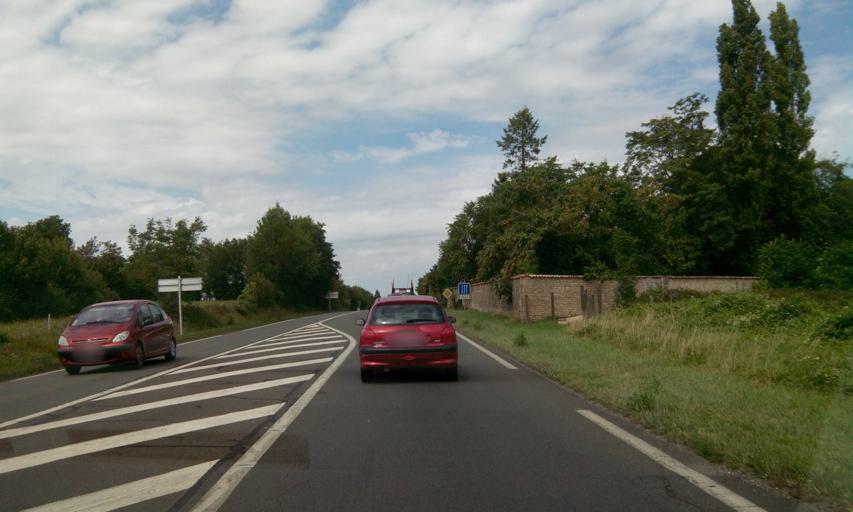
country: FR
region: Poitou-Charentes
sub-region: Departement des Deux-Sevres
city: Melle
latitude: 46.2285
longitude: -0.1602
